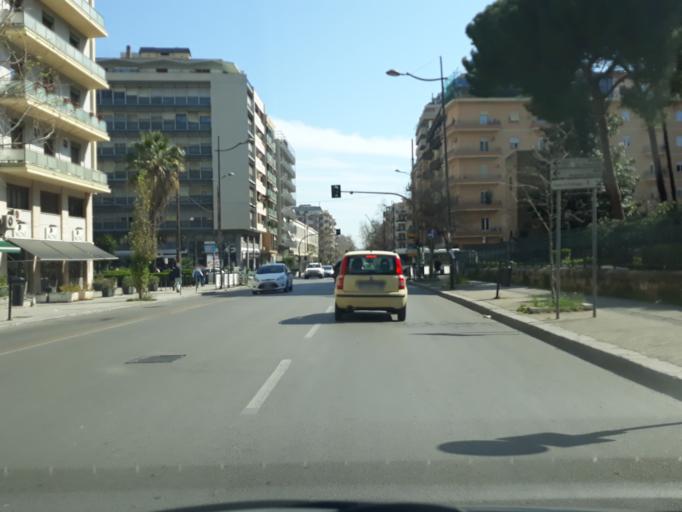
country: IT
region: Sicily
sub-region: Palermo
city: Palermo
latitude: 38.1345
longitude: 13.3509
